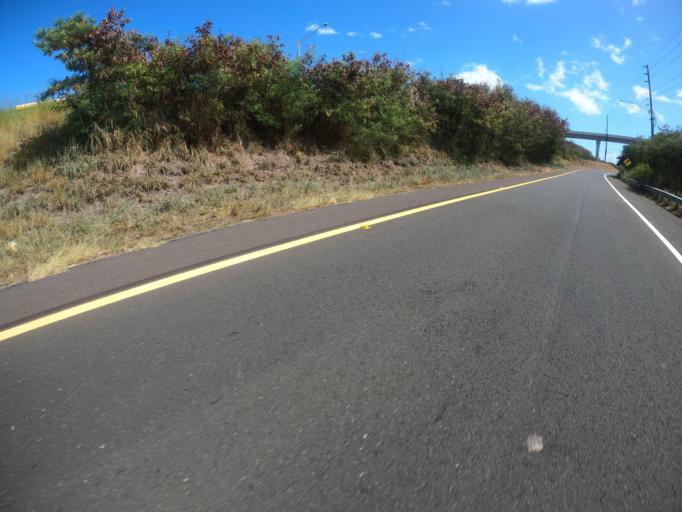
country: US
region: Hawaii
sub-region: Honolulu County
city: Royal Kunia
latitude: 21.3775
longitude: -158.0275
